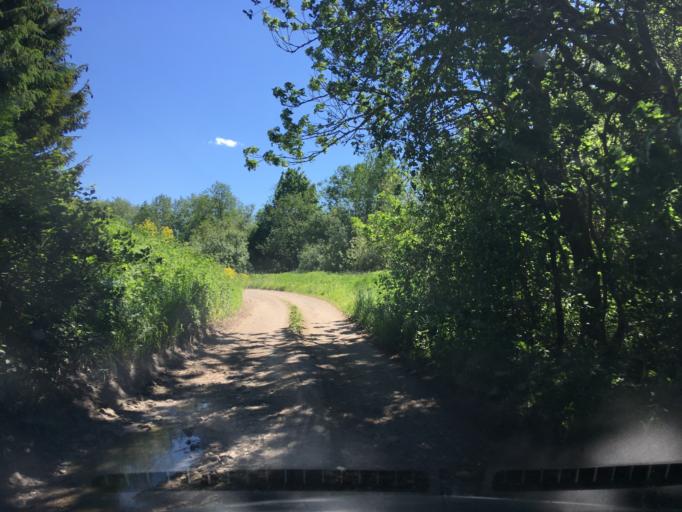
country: EE
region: Harju
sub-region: Rae vald
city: Vaida
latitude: 59.1578
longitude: 25.1303
